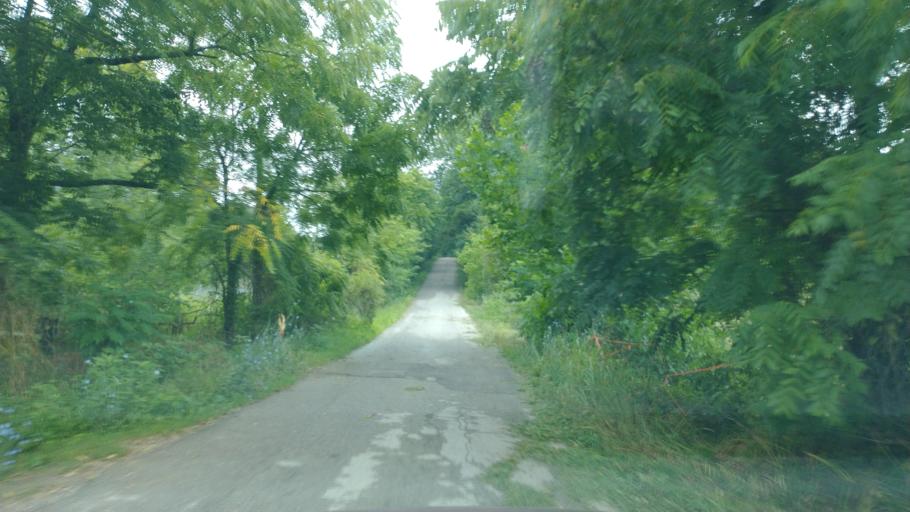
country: US
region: West Virginia
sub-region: Mason County
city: New Haven
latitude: 38.9249
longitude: -81.9794
